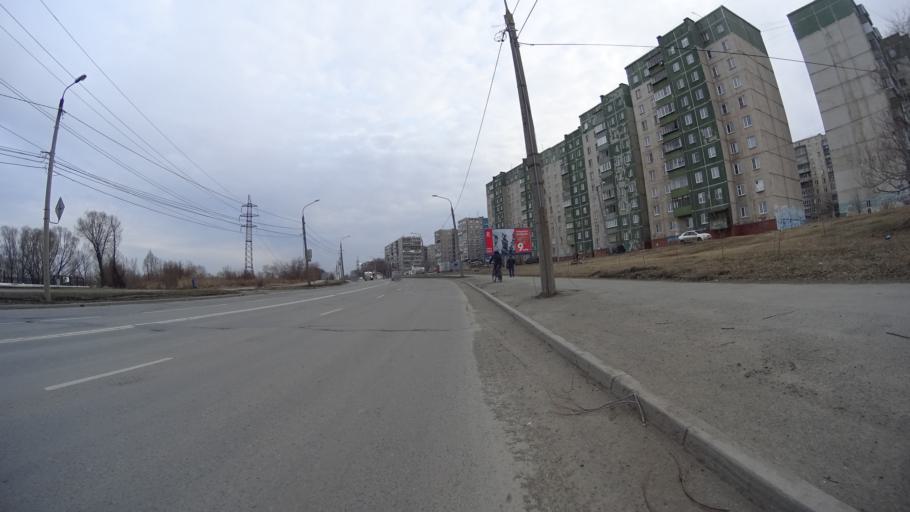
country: RU
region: Chelyabinsk
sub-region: Gorod Chelyabinsk
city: Chelyabinsk
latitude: 55.1862
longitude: 61.4845
